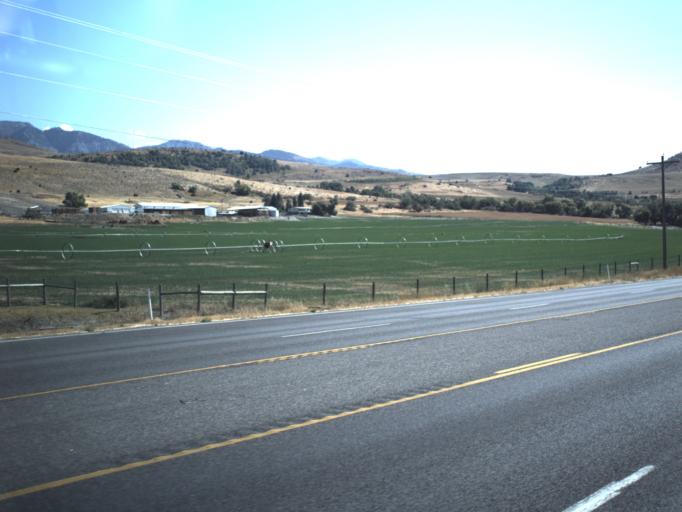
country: US
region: Utah
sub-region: Cache County
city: Richmond
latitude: 41.8946
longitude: -111.8150
